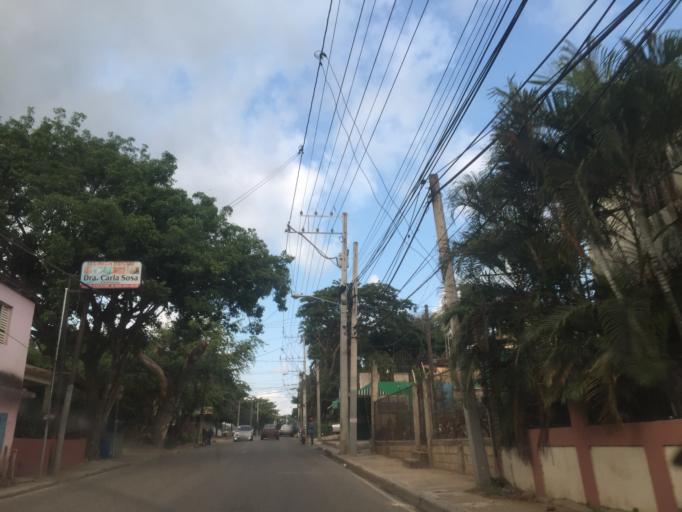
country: DO
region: Santiago
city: Santiago de los Caballeros
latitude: 19.4113
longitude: -70.7181
